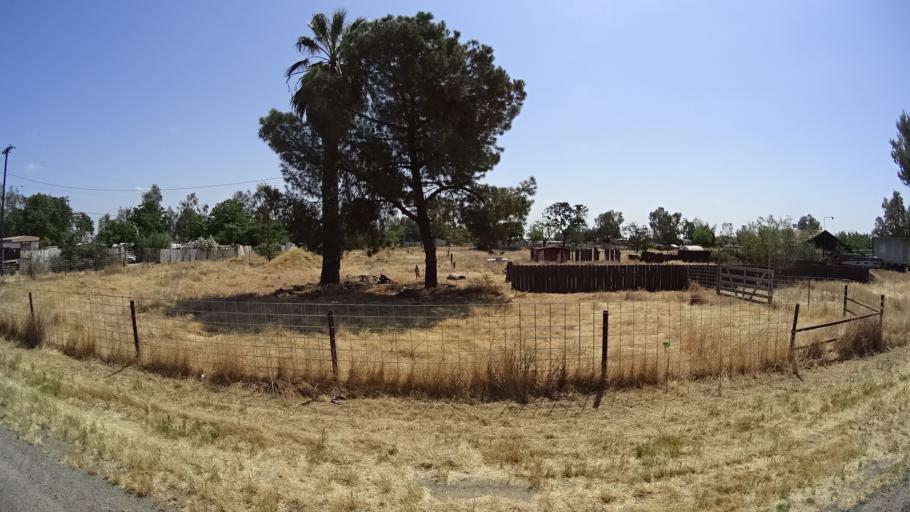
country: US
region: California
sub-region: Kings County
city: Home Garden
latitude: 36.3034
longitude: -119.6190
